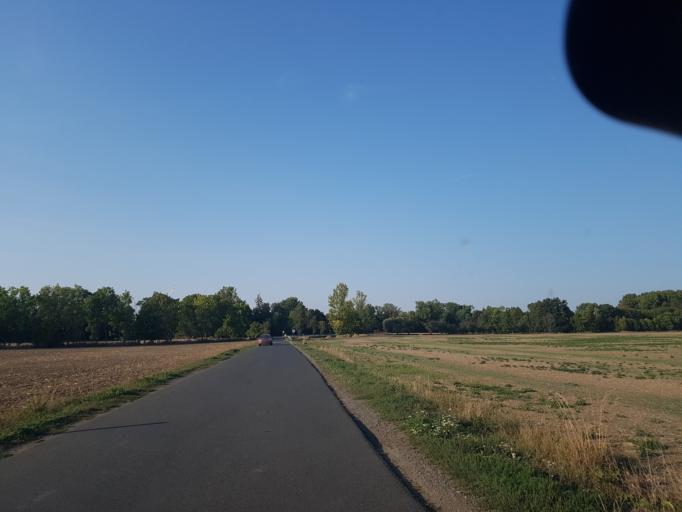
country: DE
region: Saxony
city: Stauchitz
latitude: 51.2568
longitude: 13.2282
